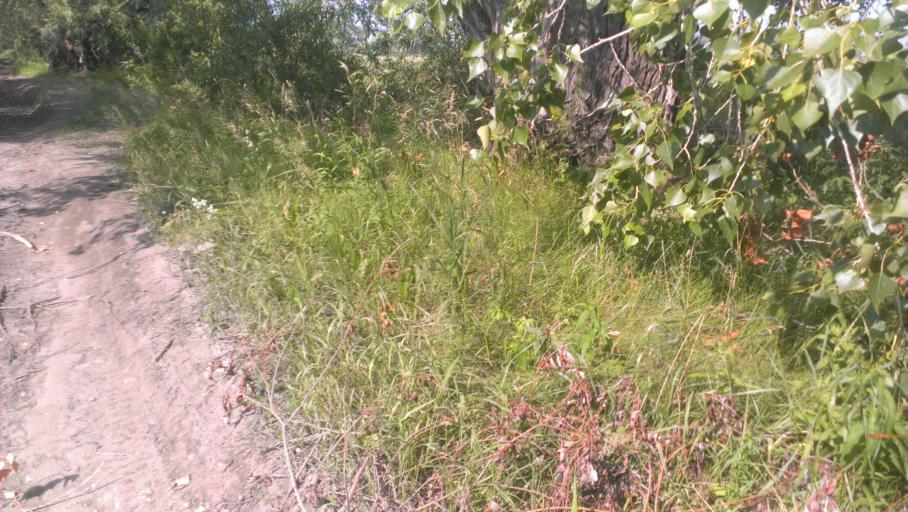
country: RU
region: Altai Krai
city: Novoaltaysk
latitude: 53.3747
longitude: 83.8569
